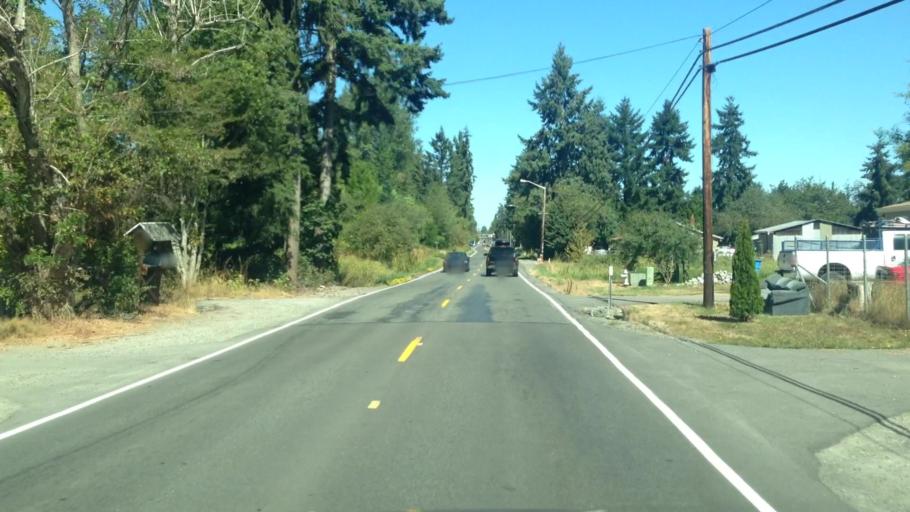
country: US
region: Washington
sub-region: Pierce County
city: Parkland
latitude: 47.1508
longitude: -122.4155
